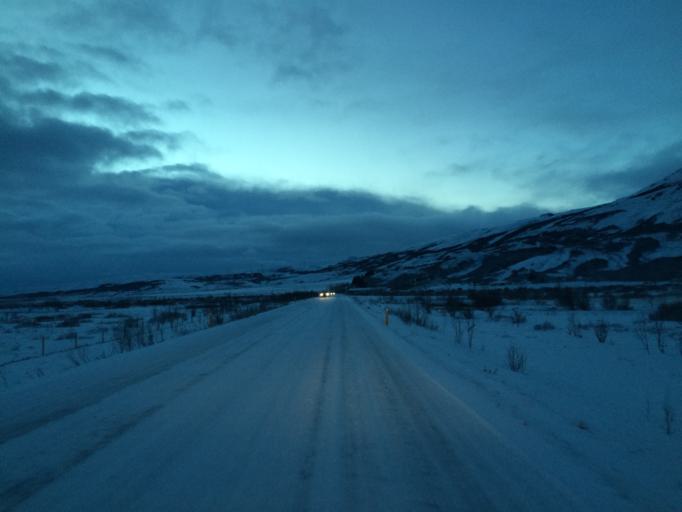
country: IS
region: South
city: Selfoss
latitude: 64.3074
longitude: -20.3127
